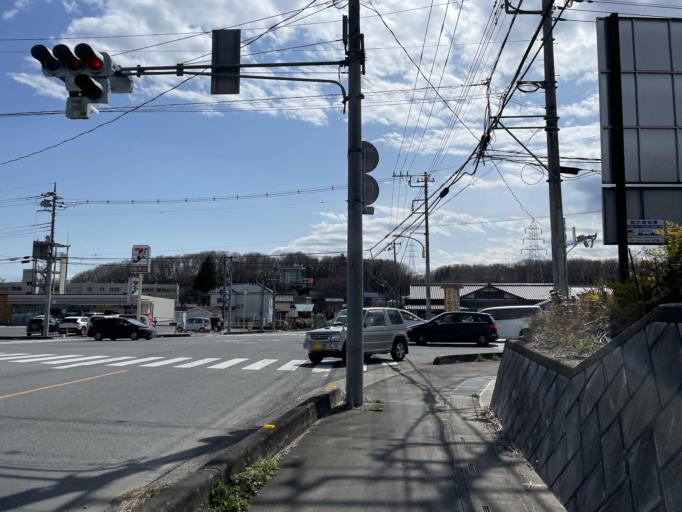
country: JP
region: Saitama
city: Morohongo
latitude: 35.9863
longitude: 139.3322
